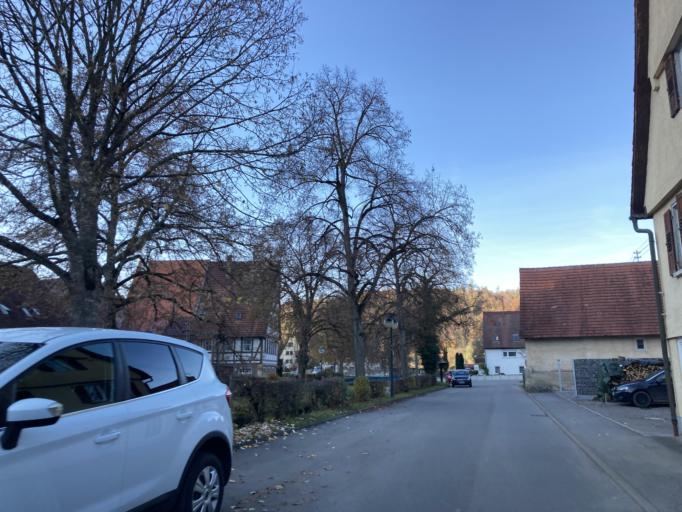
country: DE
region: Baden-Wuerttemberg
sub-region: Tuebingen Region
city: Rottenburg
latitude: 48.4562
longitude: 8.9006
